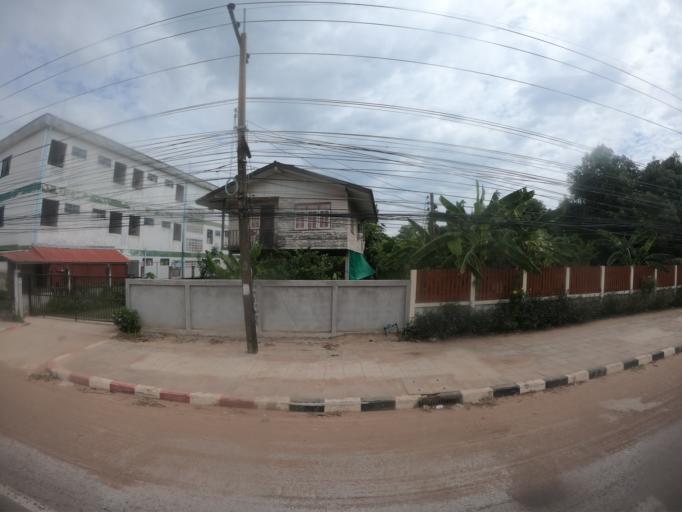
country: TH
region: Maha Sarakham
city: Maha Sarakham
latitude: 16.2382
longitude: 103.2706
